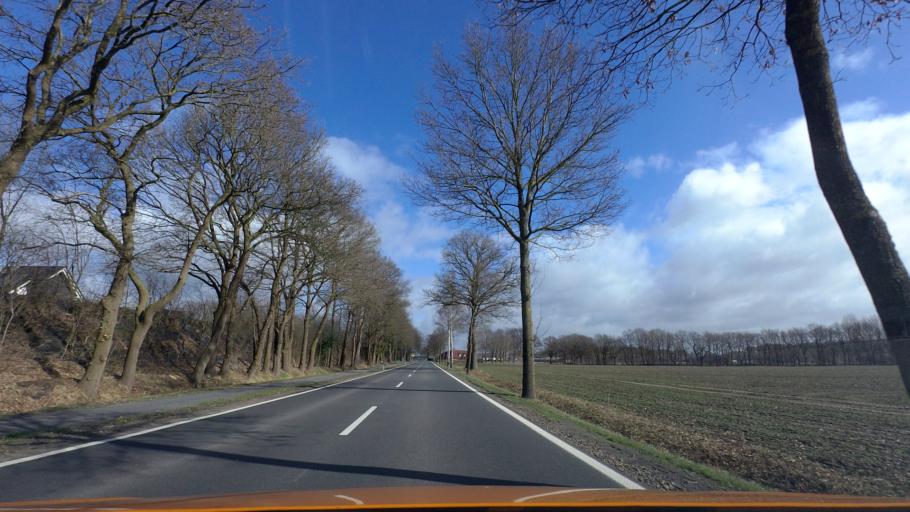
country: DE
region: Lower Saxony
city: Bosel
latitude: 53.0004
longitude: 7.9604
